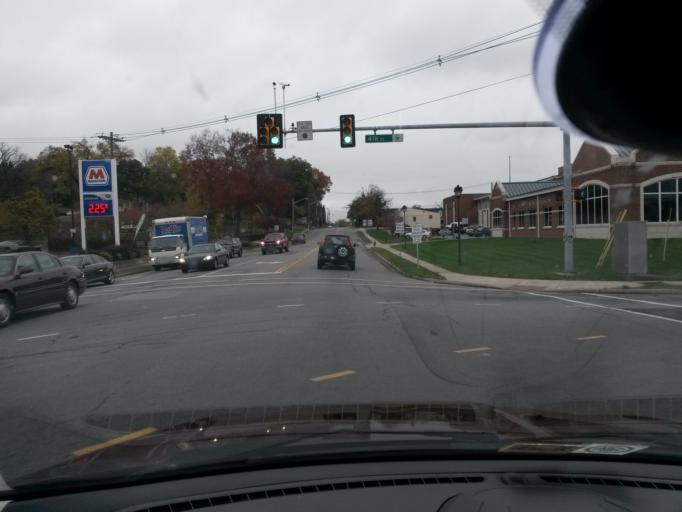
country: US
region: Virginia
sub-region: City of Salem
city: Salem
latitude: 37.2906
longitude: -80.0715
